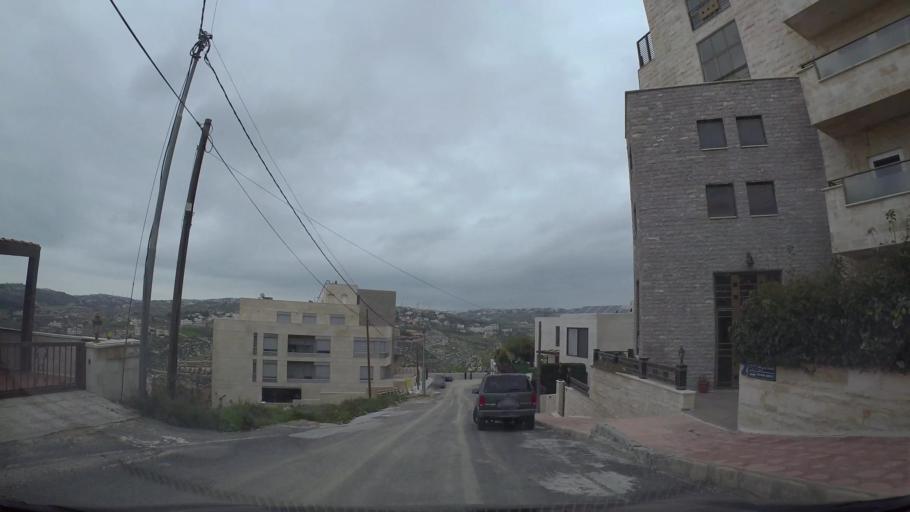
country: JO
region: Amman
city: Wadi as Sir
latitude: 31.9666
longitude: 35.8229
